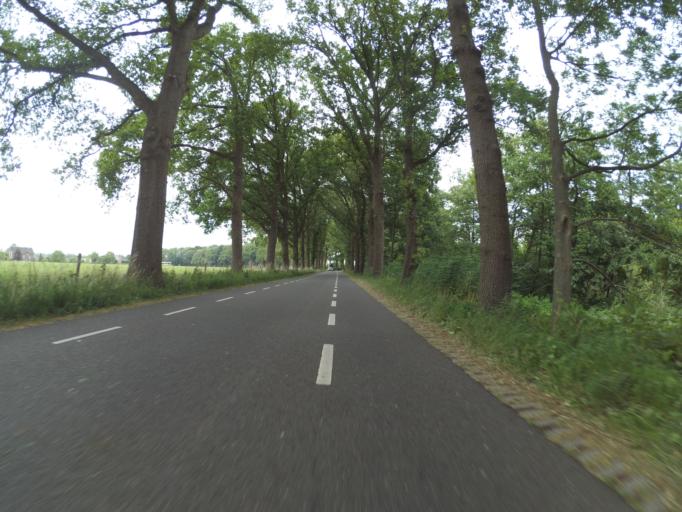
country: NL
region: Gelderland
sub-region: Gemeente Voorst
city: Voorst
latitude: 52.1470
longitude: 6.1411
